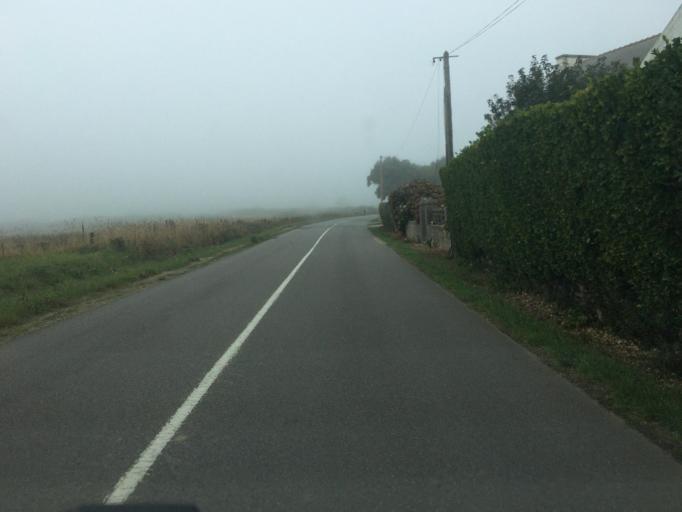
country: FR
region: Brittany
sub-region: Departement du Finistere
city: Plogoff
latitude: 48.0630
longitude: -4.6301
